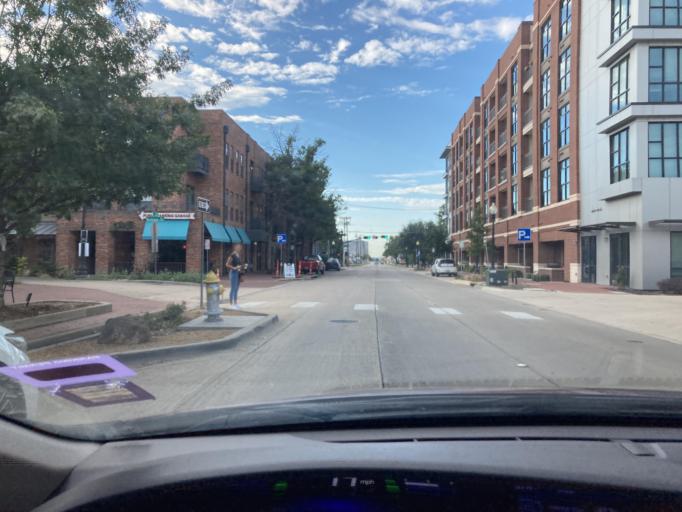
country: US
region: Texas
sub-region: Collin County
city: Plano
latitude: 33.0194
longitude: -96.6992
